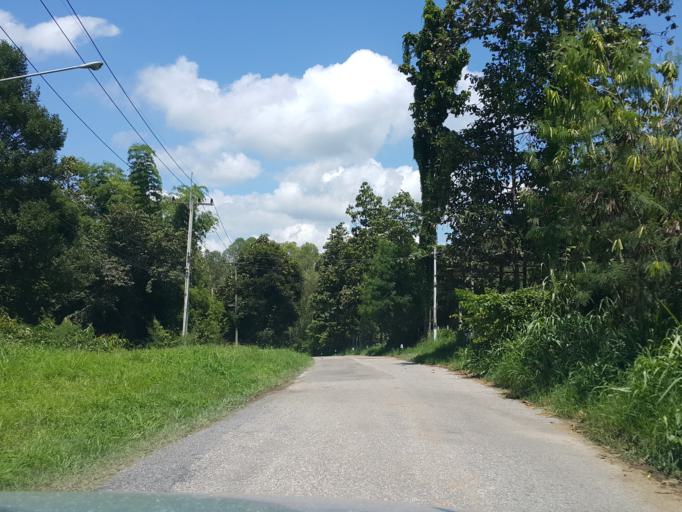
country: TH
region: Chiang Mai
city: San Kamphaeng
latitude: 18.7072
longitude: 99.1808
